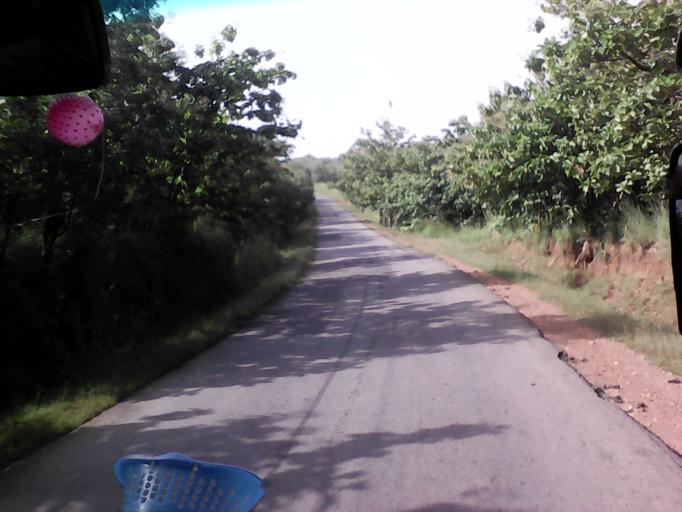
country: TG
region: Centrale
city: Sokode
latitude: 9.1307
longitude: 1.1484
